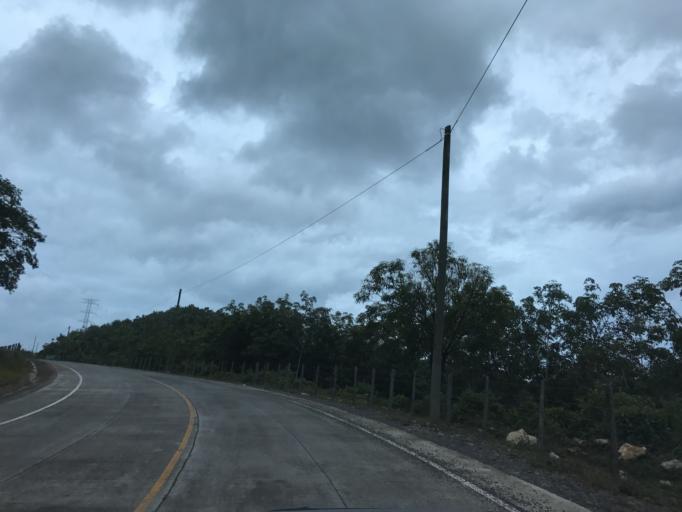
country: GT
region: Izabal
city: Morales
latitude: 15.6331
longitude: -89.0488
